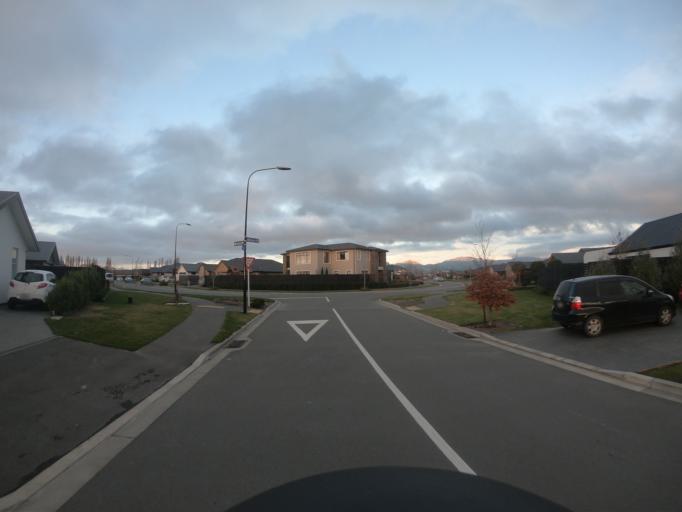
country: NZ
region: Canterbury
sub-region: Selwyn District
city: Prebbleton
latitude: -43.5640
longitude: 172.5576
